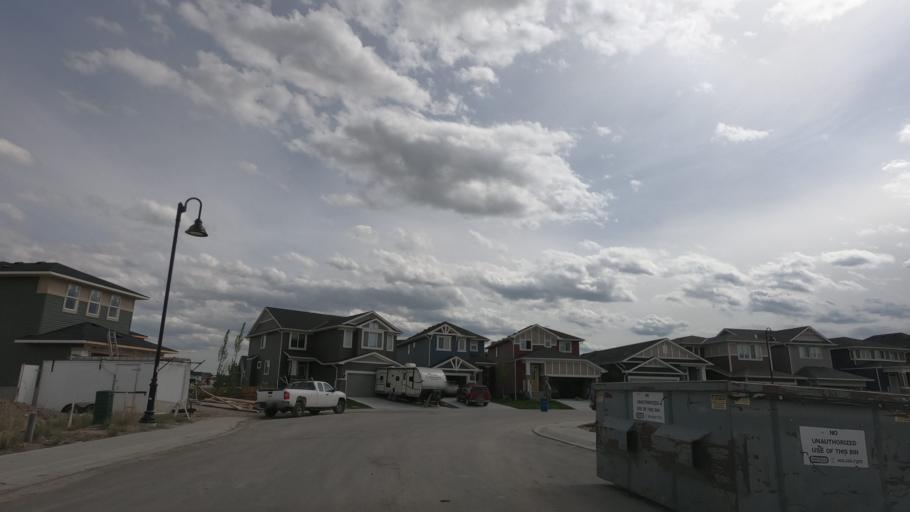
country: CA
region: Alberta
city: Airdrie
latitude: 51.2786
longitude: -114.0414
